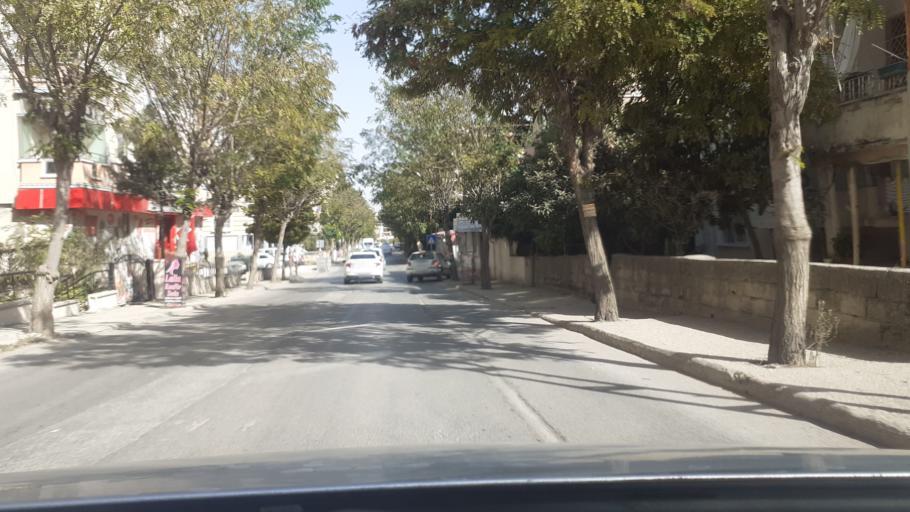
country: TR
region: Hatay
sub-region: Antakya Ilcesi
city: Antakya
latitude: 36.2109
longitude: 36.1535
